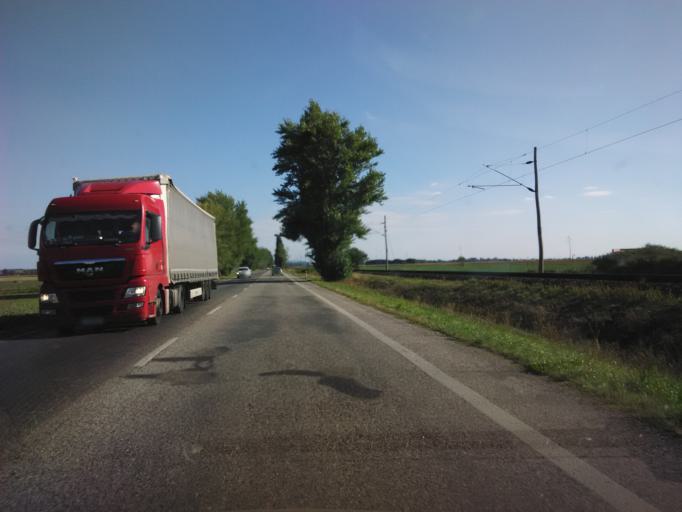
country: SK
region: Nitriansky
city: Tlmace
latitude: 48.2753
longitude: 18.5551
